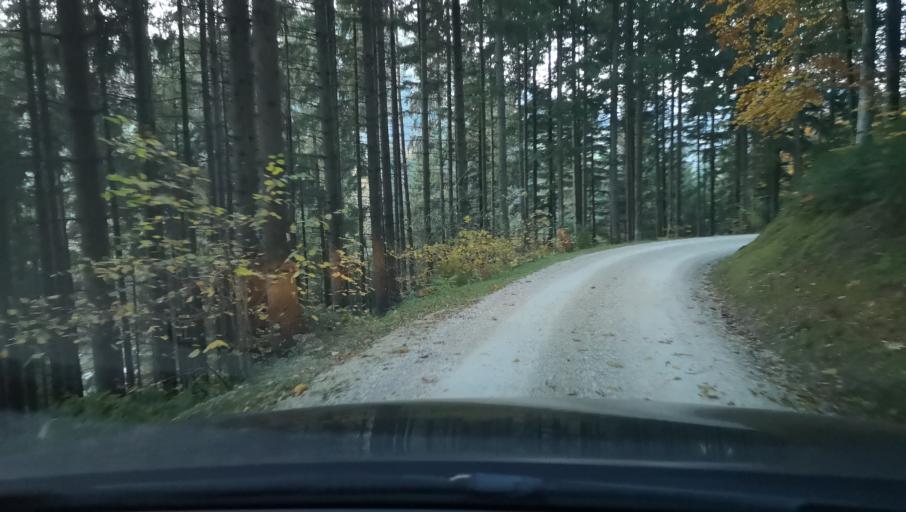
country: AT
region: Styria
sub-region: Politischer Bezirk Weiz
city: Birkfeld
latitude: 47.3653
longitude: 15.6564
